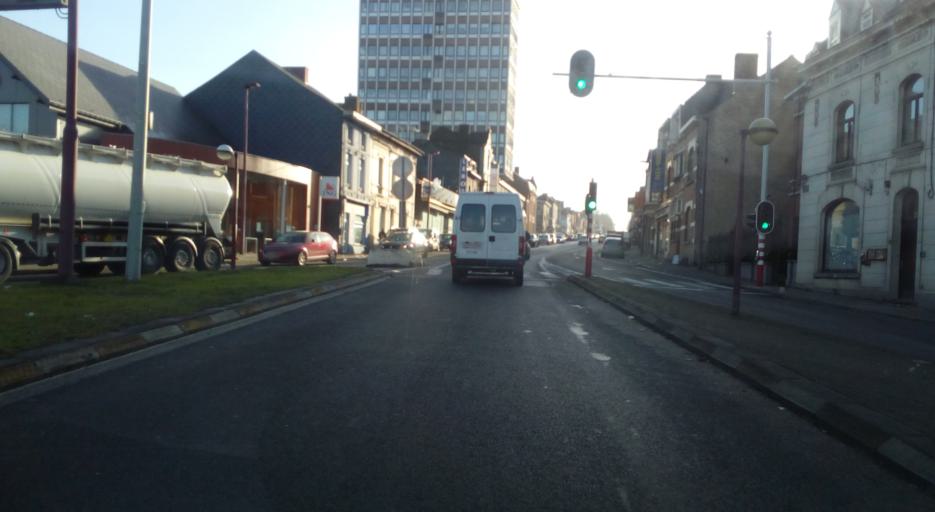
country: BE
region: Wallonia
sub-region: Province du Hainaut
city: Charleroi
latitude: 50.3828
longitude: 4.4652
